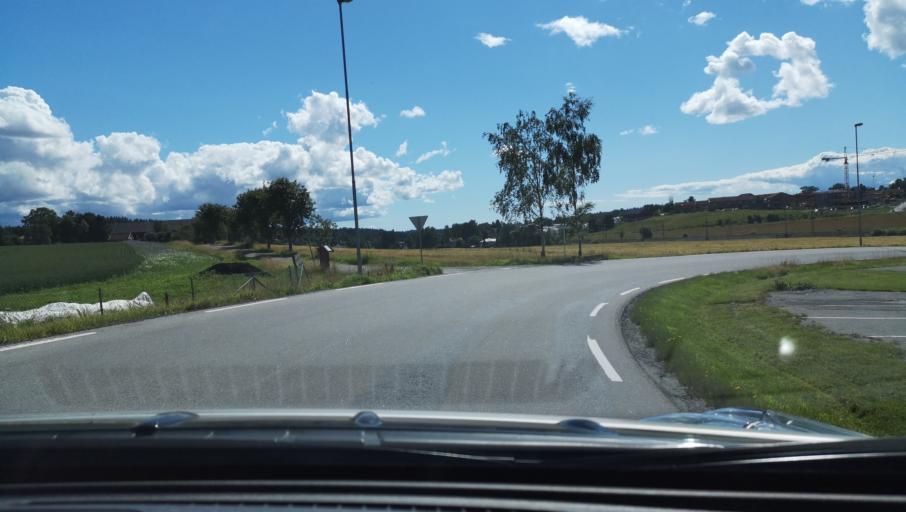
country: NO
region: Akershus
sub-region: As
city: As
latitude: 59.6621
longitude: 10.7990
